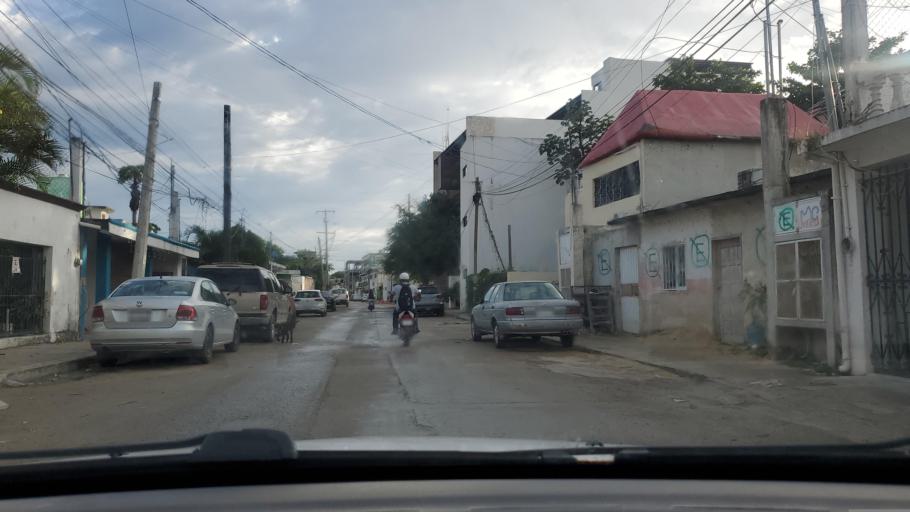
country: MX
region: Quintana Roo
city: Tulum
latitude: 20.2128
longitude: -87.4605
